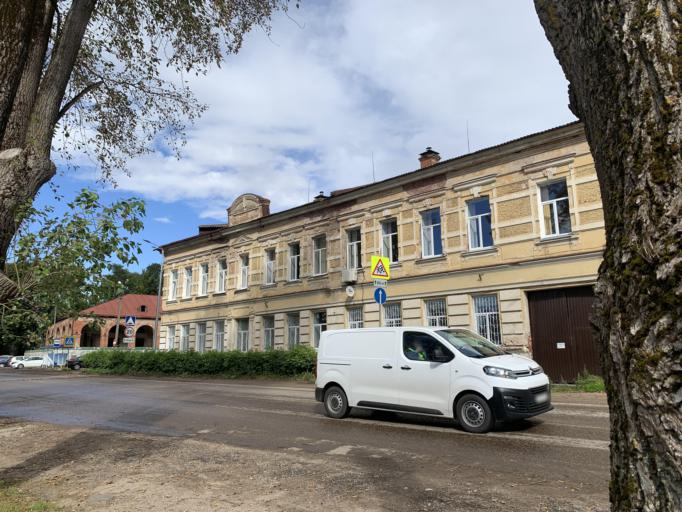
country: RU
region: Tverskaya
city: Vyshniy Volochek
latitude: 57.5808
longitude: 34.5582
